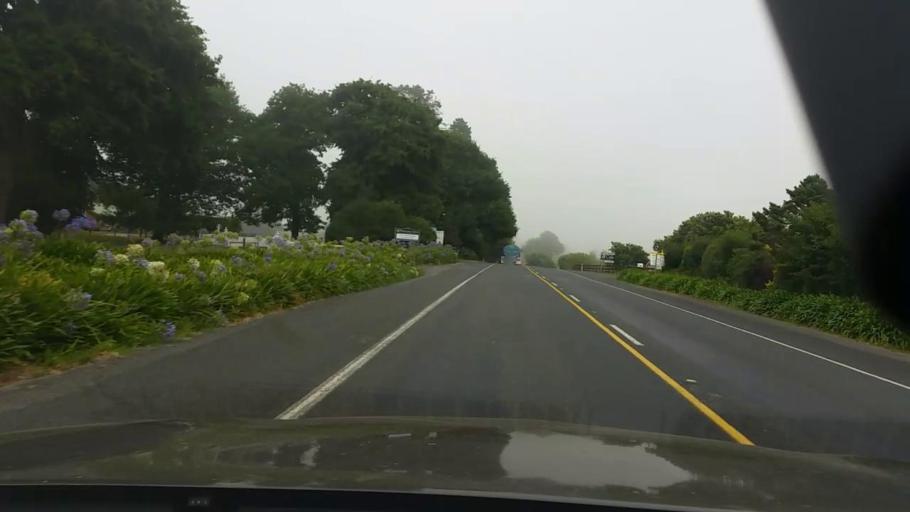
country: NZ
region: Waikato
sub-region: Hamilton City
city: Hamilton
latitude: -37.6526
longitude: 175.2968
